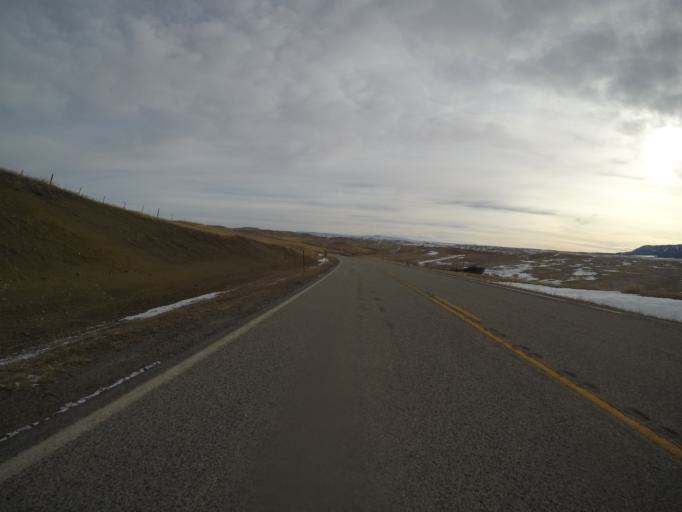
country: US
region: Montana
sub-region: Stillwater County
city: Absarokee
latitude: 45.3154
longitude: -109.4300
